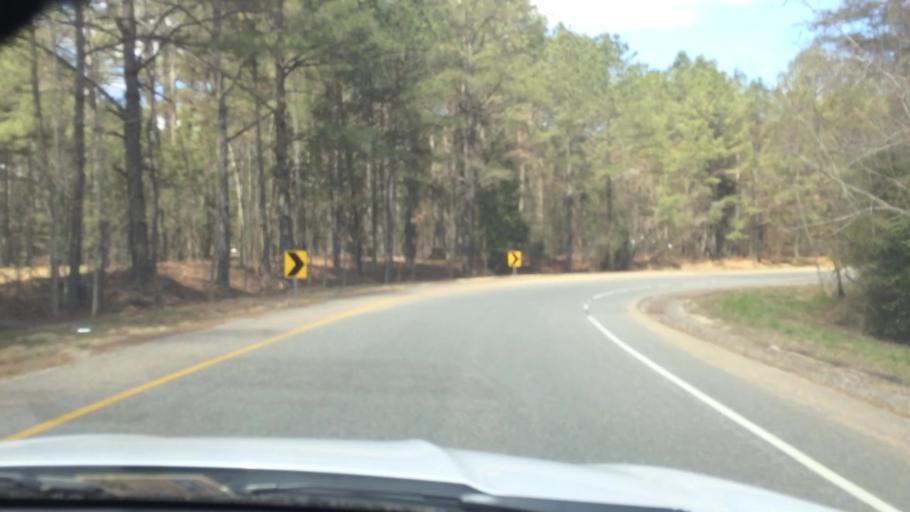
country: US
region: Virginia
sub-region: King William County
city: West Point
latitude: 37.4201
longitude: -76.8255
